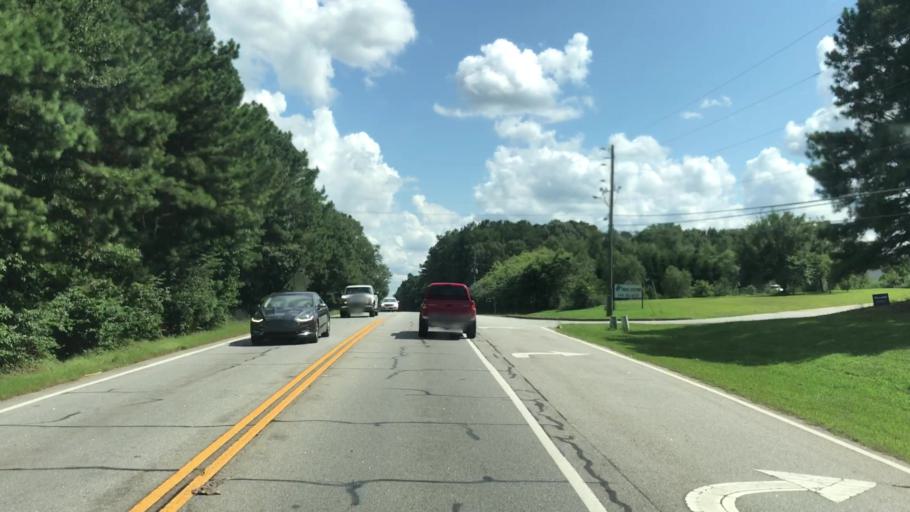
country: US
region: Georgia
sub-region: Walton County
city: Walnut Grove
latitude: 33.7229
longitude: -83.8525
